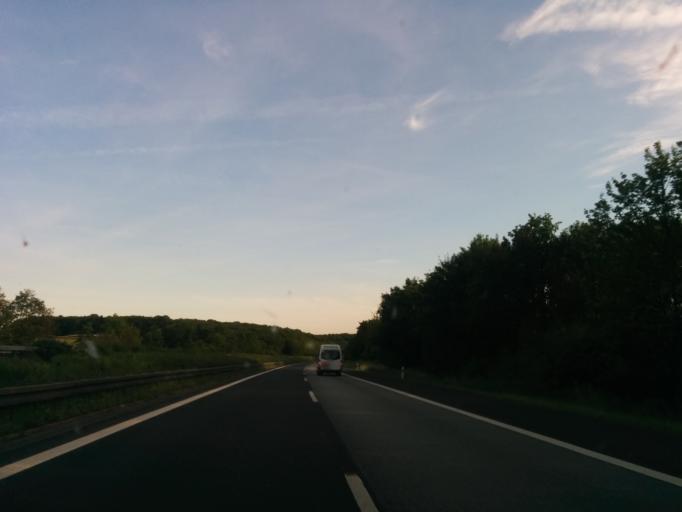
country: DE
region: Bavaria
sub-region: Regierungsbezirk Unterfranken
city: Werneck
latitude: 50.0275
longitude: 10.0701
